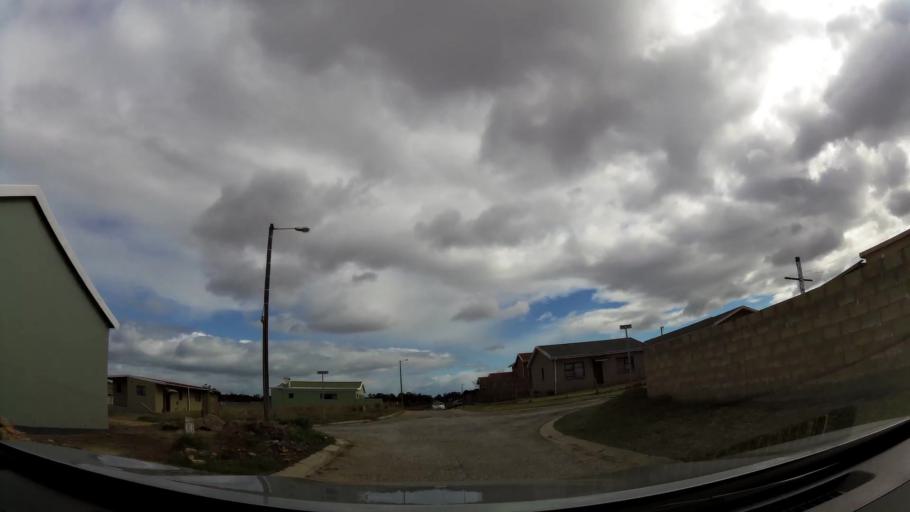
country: ZA
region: Western Cape
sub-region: Eden District Municipality
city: George
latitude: -34.0270
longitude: 22.4762
